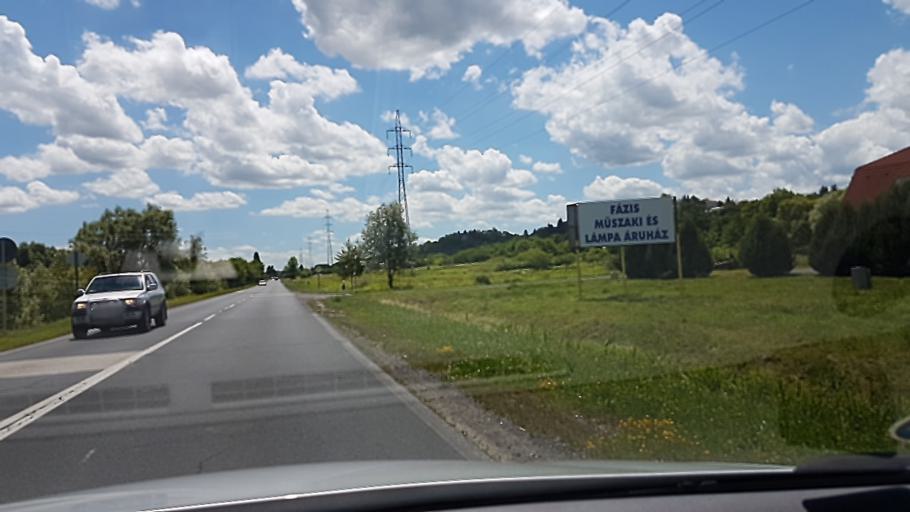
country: HU
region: Zala
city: Zalaegerszeg
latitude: 46.8364
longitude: 16.8645
